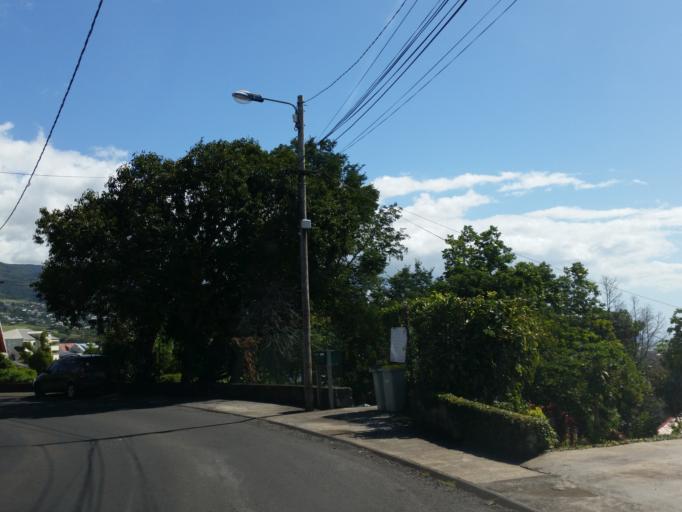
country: RE
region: Reunion
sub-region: Reunion
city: Sainte-Marie
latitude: -20.9250
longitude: 55.5243
